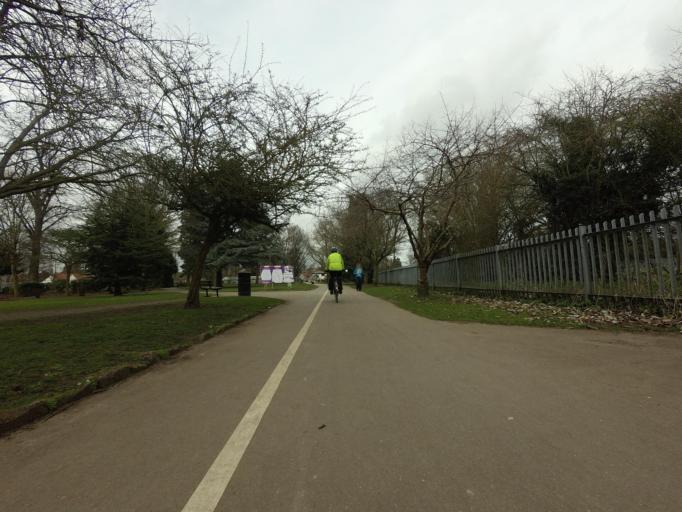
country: GB
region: England
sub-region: Lincolnshire
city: Grantham
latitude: 52.9166
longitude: -0.6371
